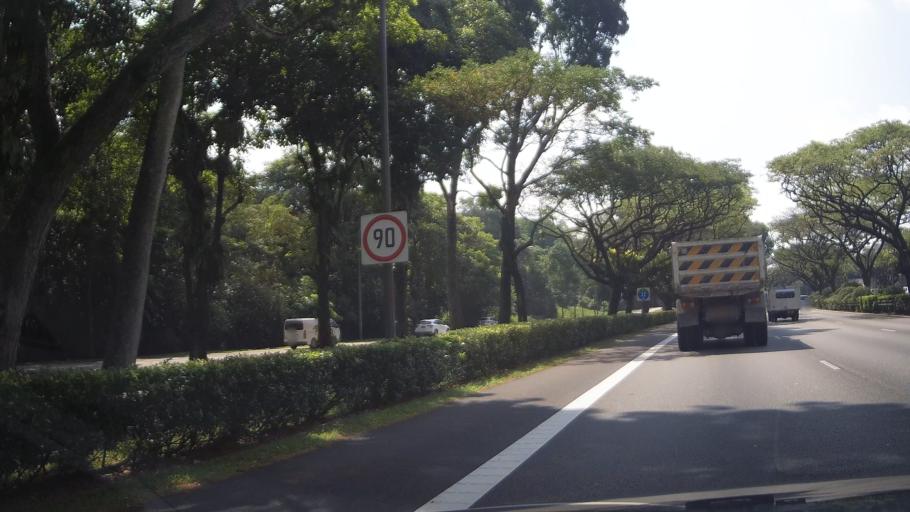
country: MY
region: Johor
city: Johor Bahru
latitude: 1.3519
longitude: 103.7312
